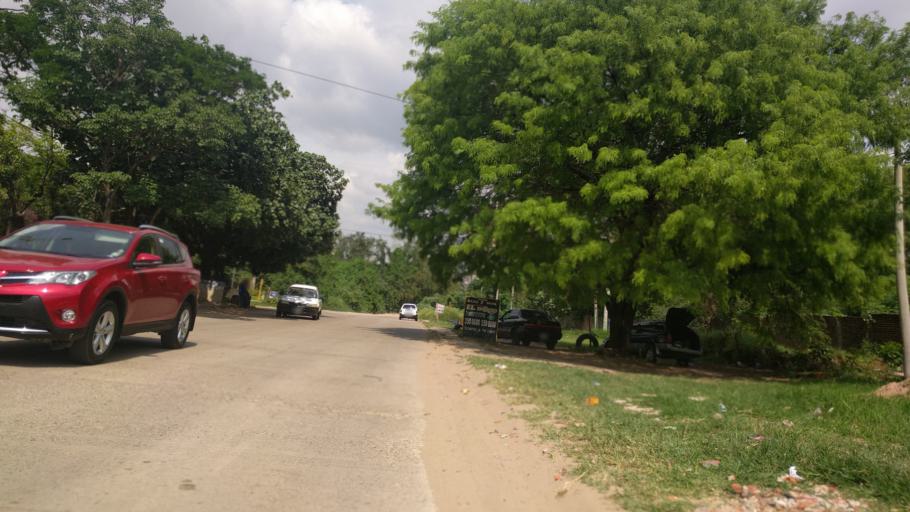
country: BO
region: Santa Cruz
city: Santa Cruz de la Sierra
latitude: -17.7925
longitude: -63.2209
